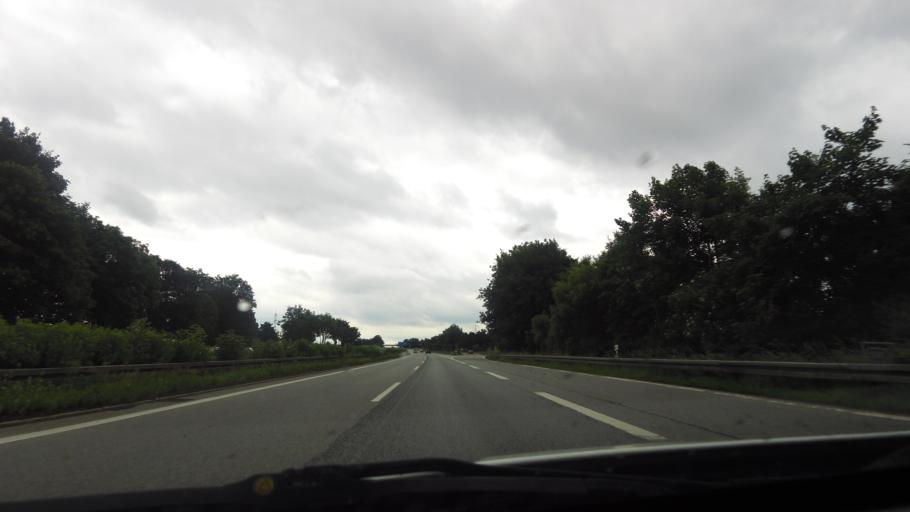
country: DE
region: Bavaria
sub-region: Swabia
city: Buxheim
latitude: 48.0152
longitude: 10.1366
